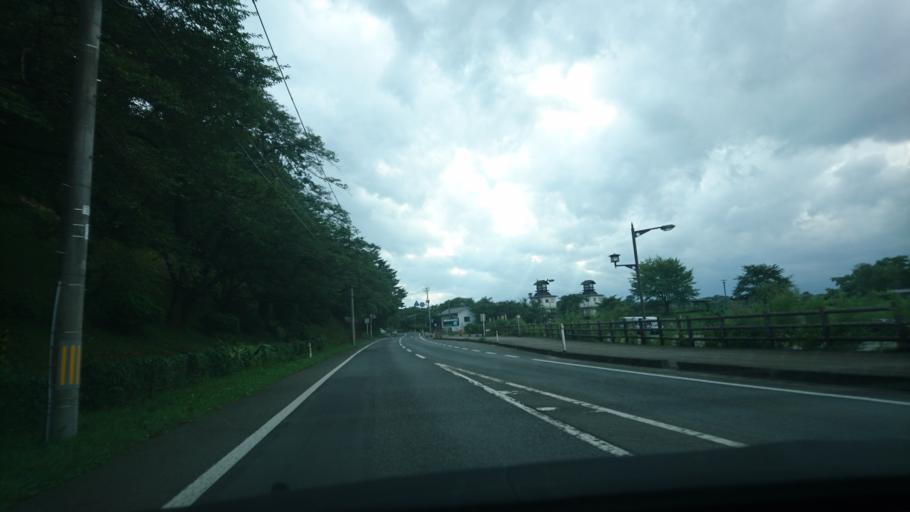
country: JP
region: Iwate
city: Kitakami
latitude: 39.2718
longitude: 141.1273
